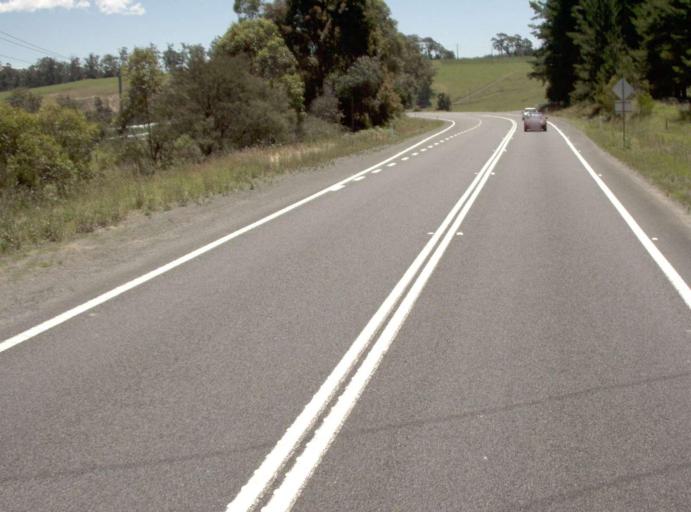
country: AU
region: Victoria
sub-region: East Gippsland
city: Lakes Entrance
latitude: -37.7034
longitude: 148.5657
